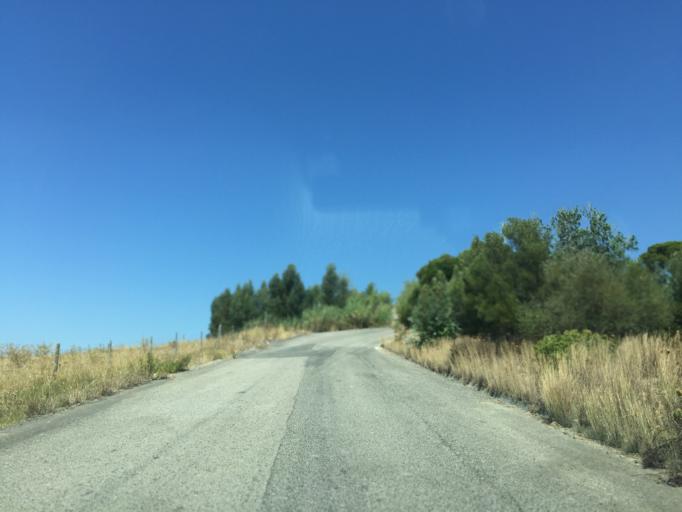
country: PT
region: Lisbon
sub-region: Alenquer
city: Carregado
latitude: 39.0452
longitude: -8.9284
